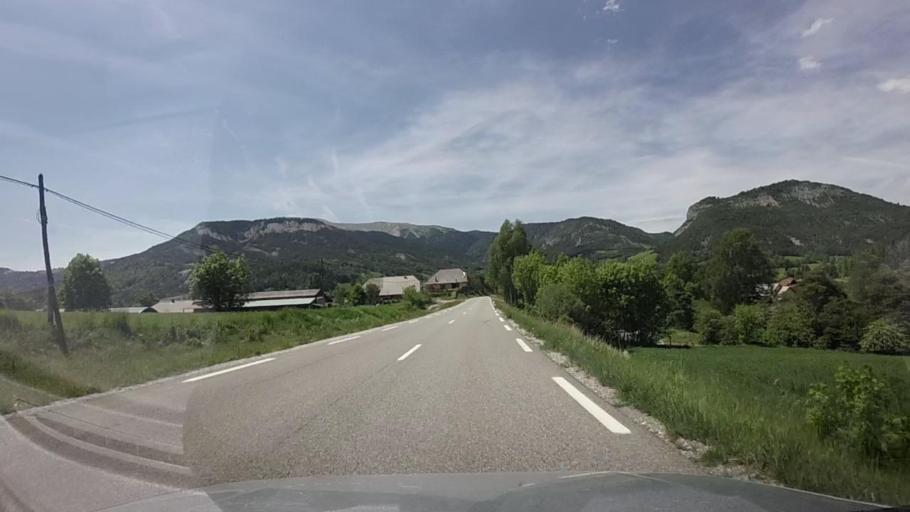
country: FR
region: Provence-Alpes-Cote d'Azur
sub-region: Departement des Alpes-de-Haute-Provence
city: Seyne-les-Alpes
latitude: 44.3731
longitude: 6.3192
